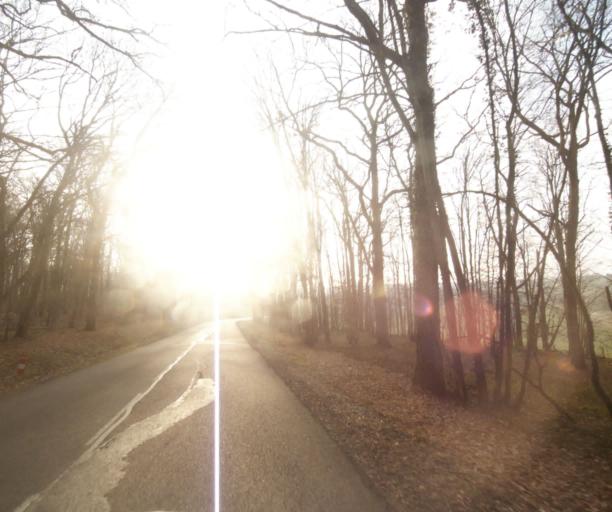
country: FR
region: Champagne-Ardenne
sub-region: Departement de la Marne
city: Sermaize-les-Bains
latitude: 48.7504
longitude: 4.9031
